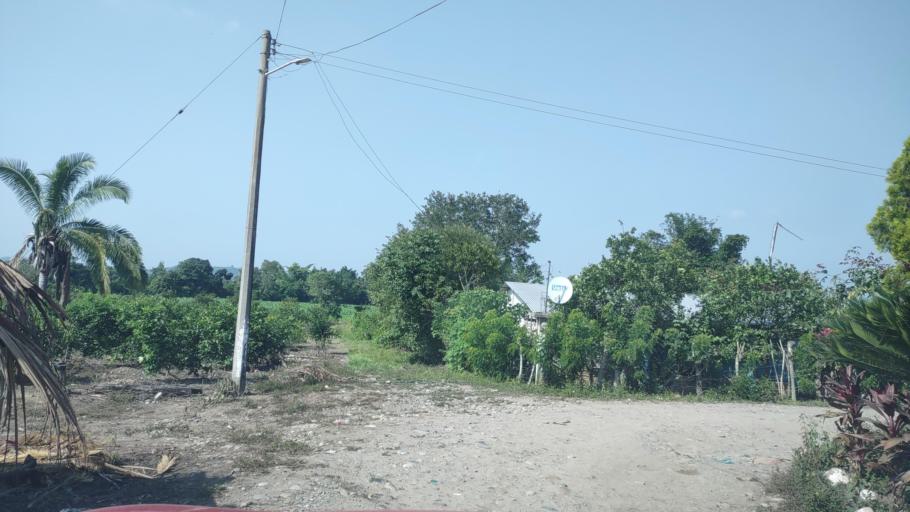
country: MX
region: Puebla
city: Espinal
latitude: 20.2403
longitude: -97.3485
